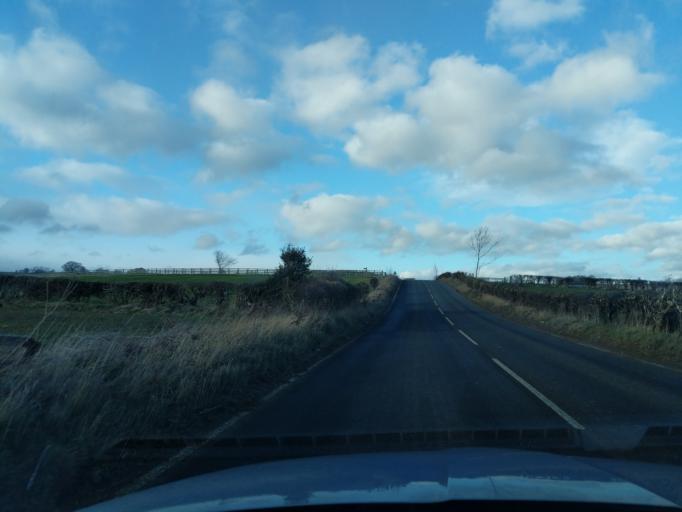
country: GB
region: England
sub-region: North Yorkshire
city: Catterick Garrison
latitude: 54.3327
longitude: -1.6854
